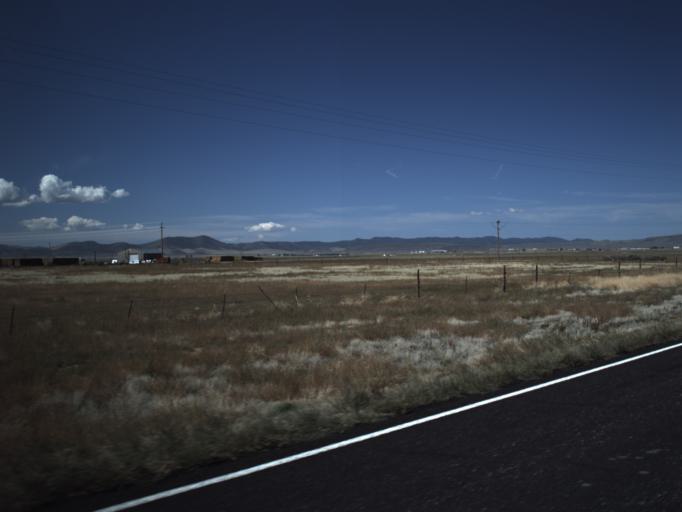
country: US
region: Utah
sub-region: Washington County
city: Enterprise
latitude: 37.6841
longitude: -113.5855
